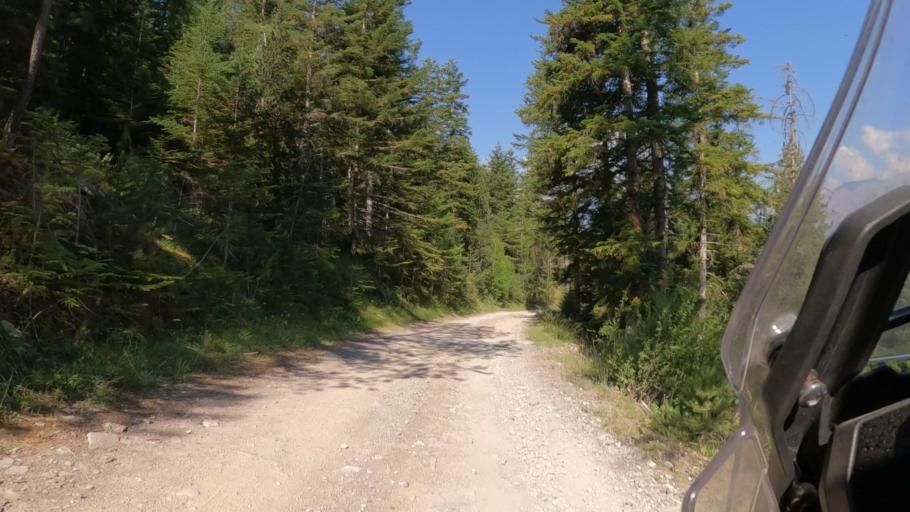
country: FR
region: Provence-Alpes-Cote d'Azur
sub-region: Departement des Hautes-Alpes
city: Embrun
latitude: 44.5882
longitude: 6.5581
